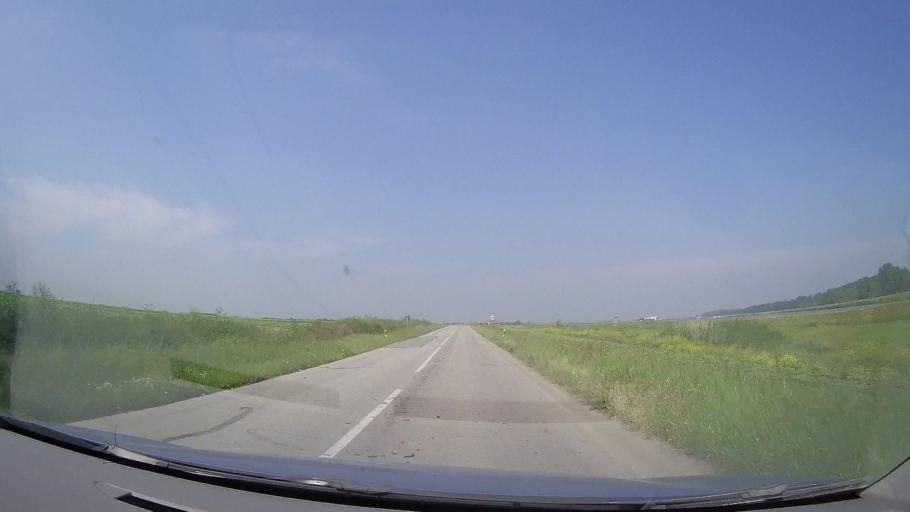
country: RS
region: Autonomna Pokrajina Vojvodina
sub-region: Srednjebanatski Okrug
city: Secanj
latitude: 45.3518
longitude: 20.7583
